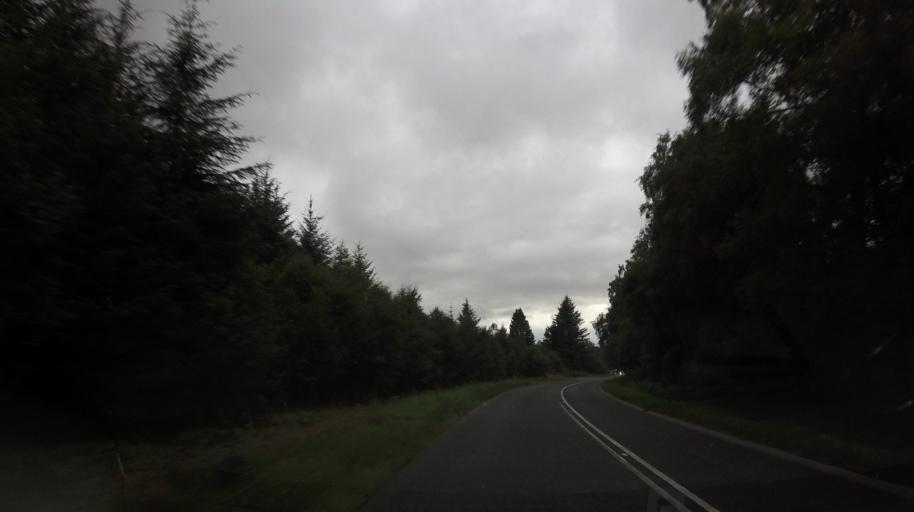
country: GB
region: Scotland
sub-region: Aberdeenshire
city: Torphins
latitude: 57.2022
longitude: -2.5975
